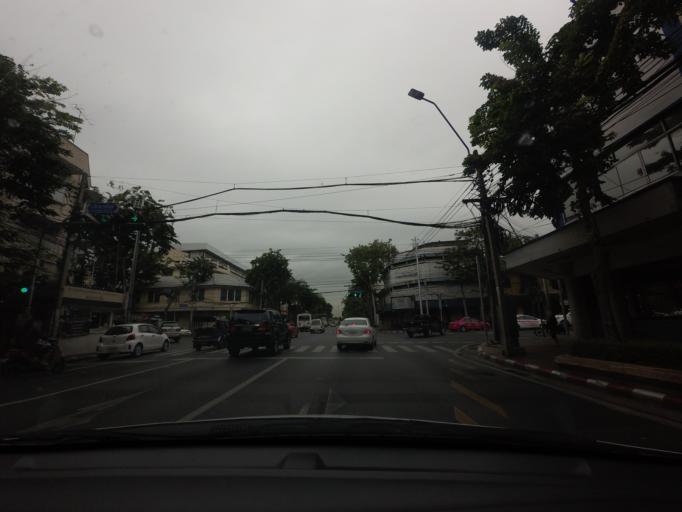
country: TH
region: Bangkok
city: Pom Prap Sattru Phai
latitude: 13.7565
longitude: 100.5099
